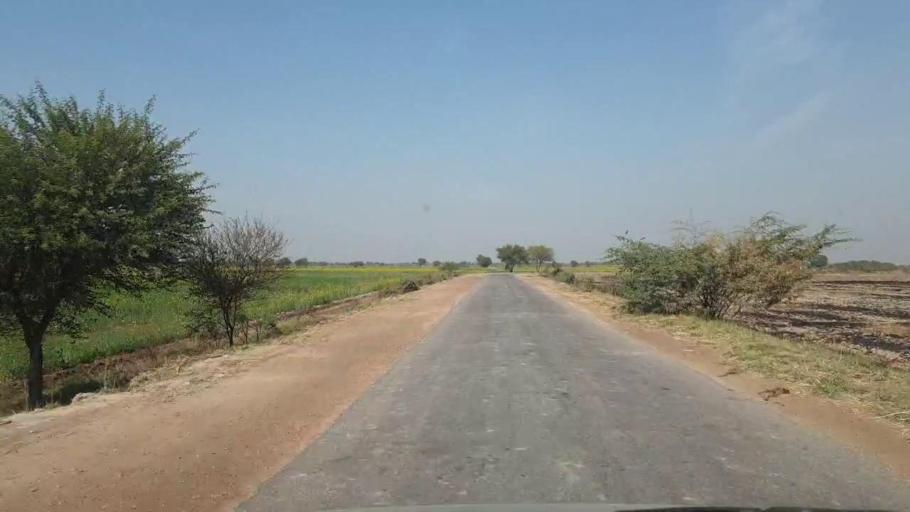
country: PK
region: Sindh
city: Chambar
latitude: 25.3162
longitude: 68.8177
